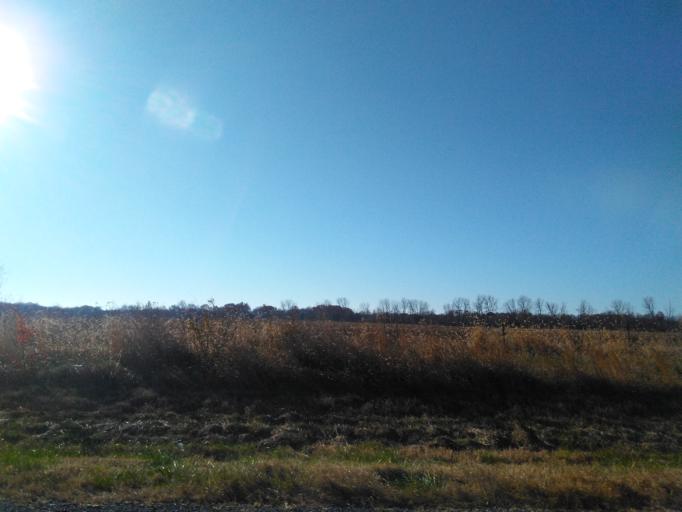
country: US
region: Illinois
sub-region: Madison County
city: Troy
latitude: 38.7554
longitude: -89.8616
